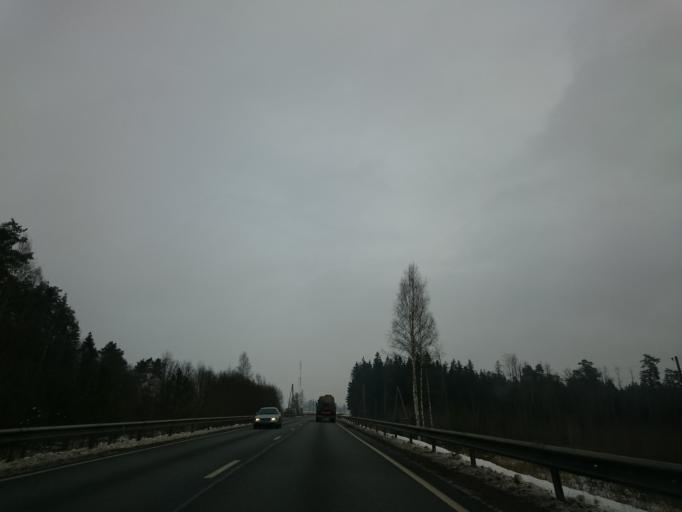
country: LV
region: Krimulda
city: Ragana
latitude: 57.2142
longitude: 24.7844
